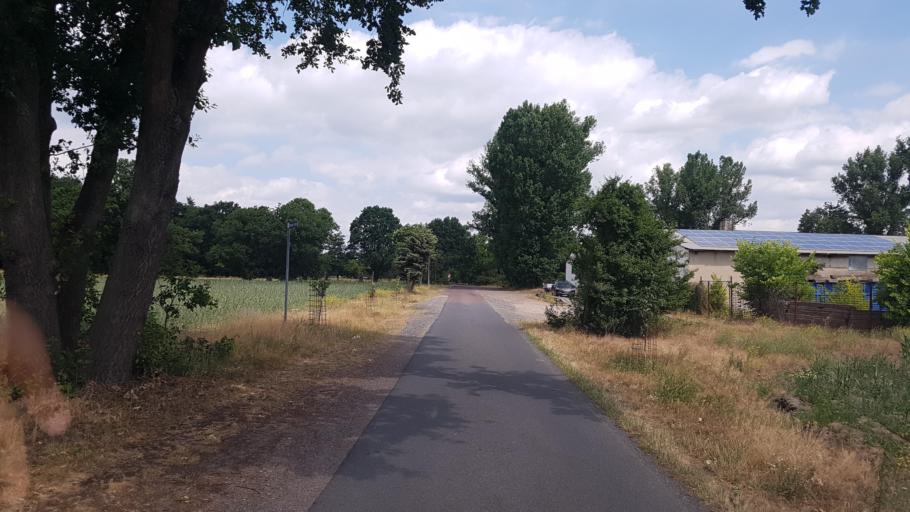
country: DE
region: Brandenburg
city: Brandenburg an der Havel
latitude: 52.3332
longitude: 12.5449
